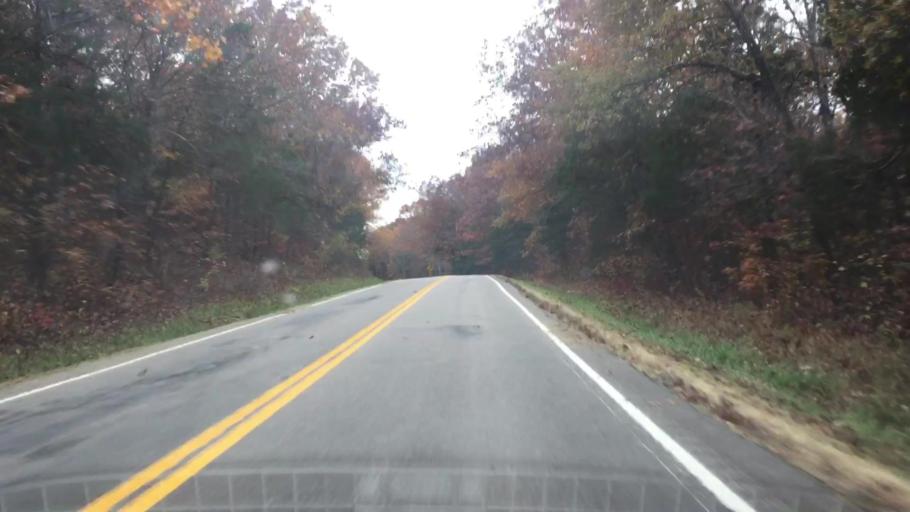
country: US
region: Missouri
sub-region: Gasconade County
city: Hermann
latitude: 38.7234
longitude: -91.6969
